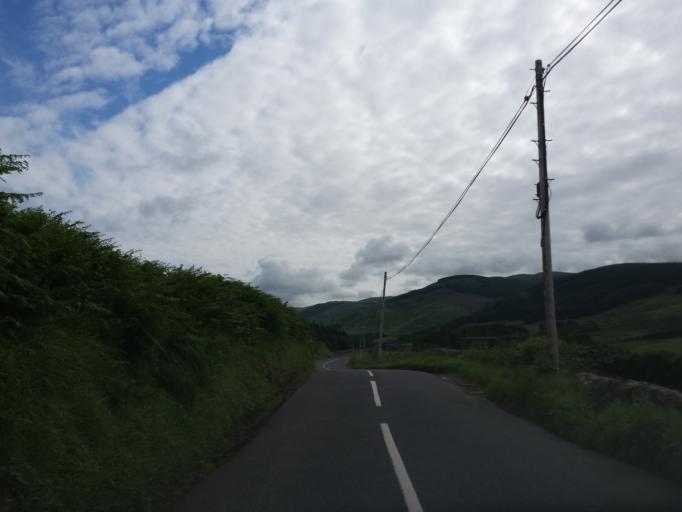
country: GB
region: Scotland
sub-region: Dumfries and Galloway
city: Moffat
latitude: 55.3262
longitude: -3.4104
